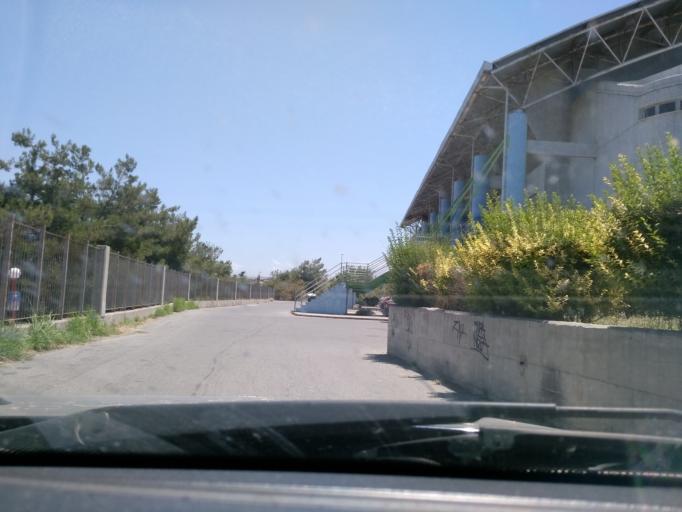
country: GR
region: Crete
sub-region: Nomos Irakleiou
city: Gazi
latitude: 35.3160
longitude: 25.1024
